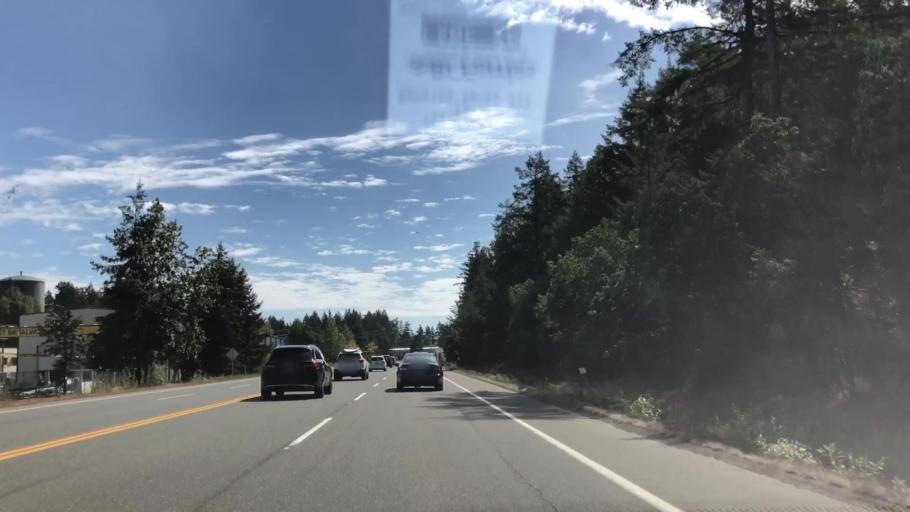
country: CA
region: British Columbia
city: Nanaimo
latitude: 49.1356
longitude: -123.8737
